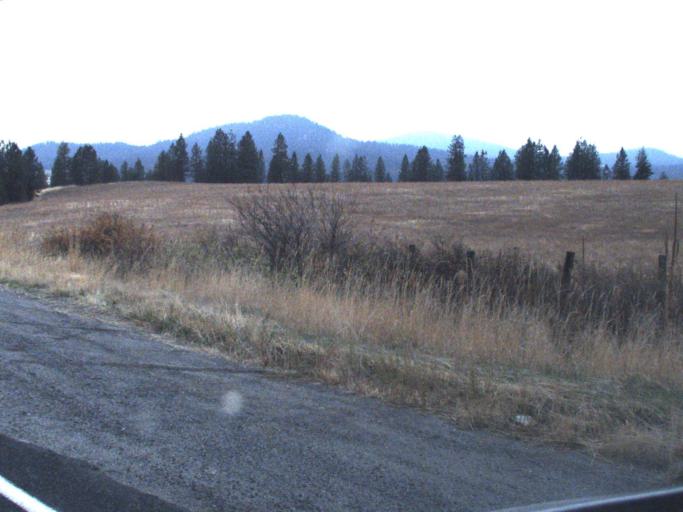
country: US
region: Washington
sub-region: Lincoln County
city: Davenport
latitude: 48.0424
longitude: -118.2248
